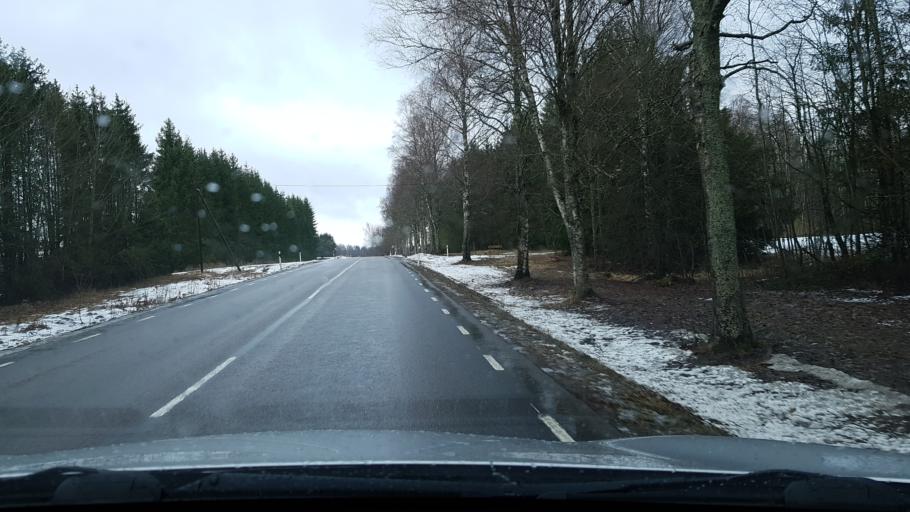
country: LV
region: Apes Novads
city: Ape
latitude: 57.6031
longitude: 26.6116
